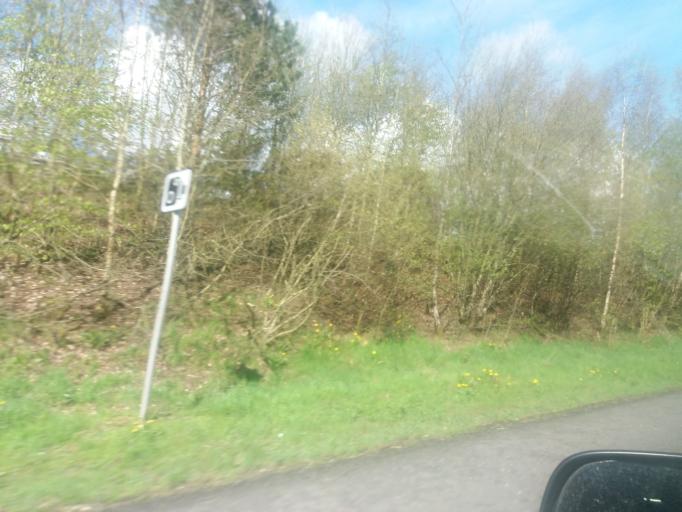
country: IE
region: Ulster
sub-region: An Cabhan
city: Cavan
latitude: 54.0397
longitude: -7.3781
